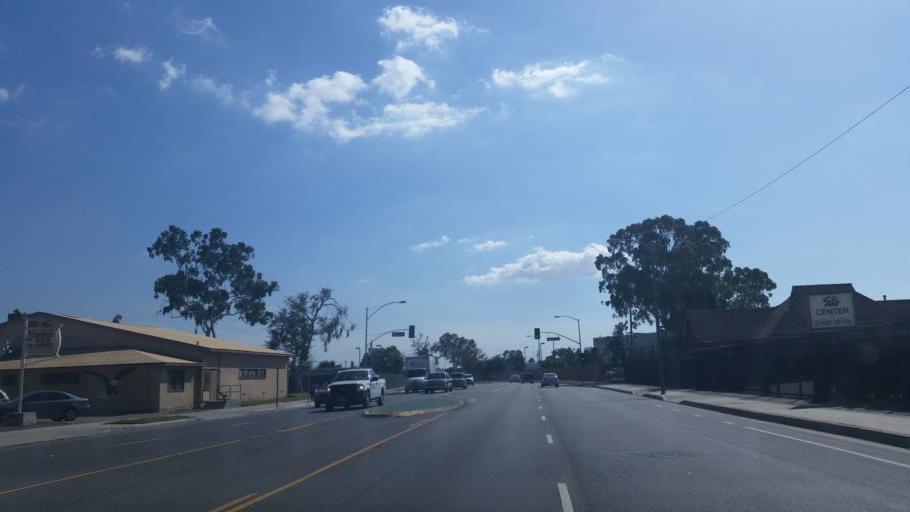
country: US
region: California
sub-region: Los Angeles County
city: Compton
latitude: 33.8932
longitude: -118.2160
